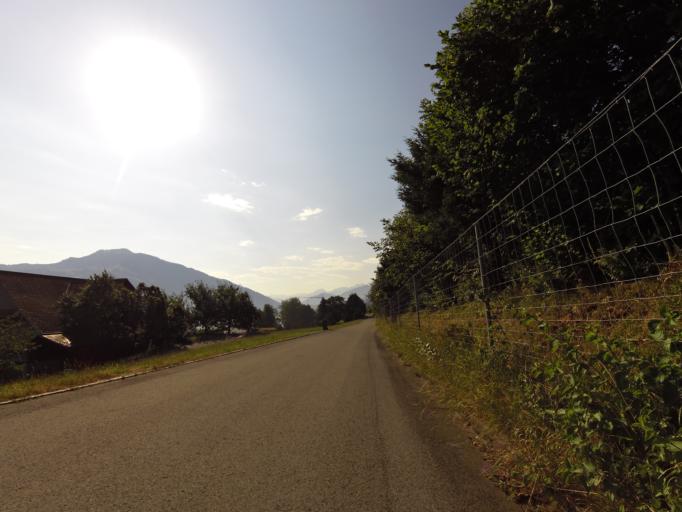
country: CH
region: Schwyz
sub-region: Bezirk Kuessnacht
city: Kussnacht
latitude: 47.0846
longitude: 8.4772
